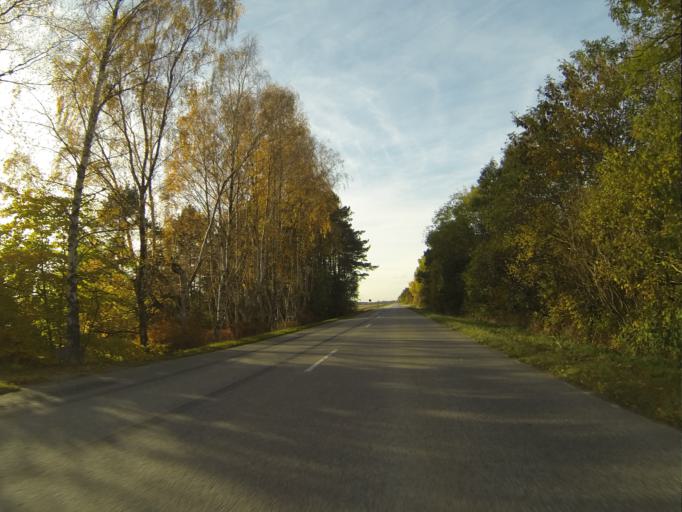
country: SE
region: Skane
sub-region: Hoors Kommun
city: Loberod
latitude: 55.7236
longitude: 13.4597
